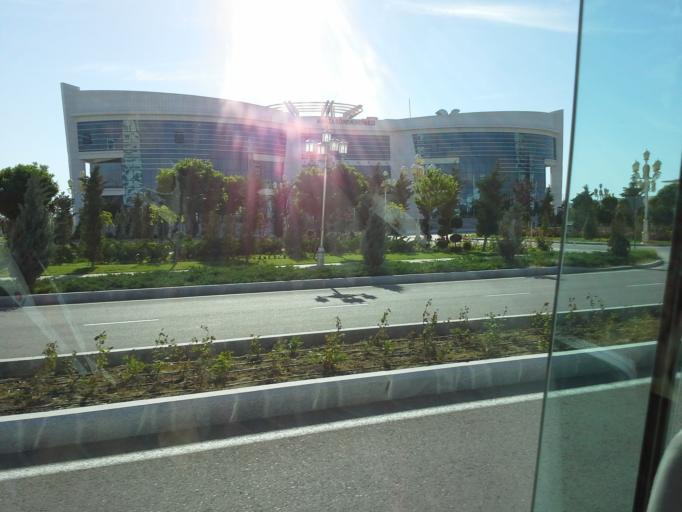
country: TM
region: Balkan
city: Turkmenbasy
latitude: 39.9784
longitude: 52.8278
